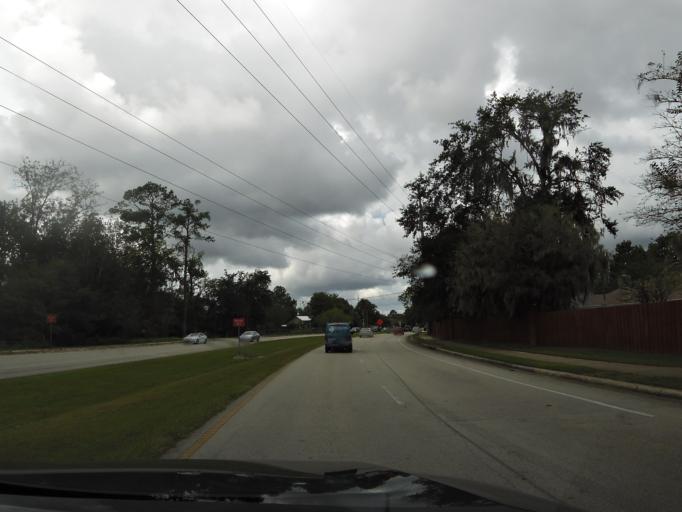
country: US
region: Florida
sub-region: Clay County
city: Lakeside
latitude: 30.0996
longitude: -81.7491
